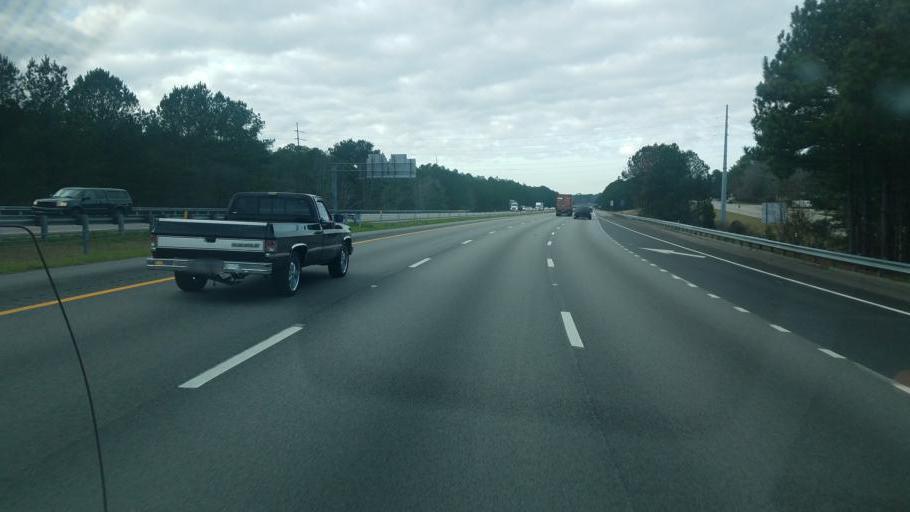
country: US
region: South Carolina
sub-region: Richland County
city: Woodfield
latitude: 34.0503
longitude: -80.9241
